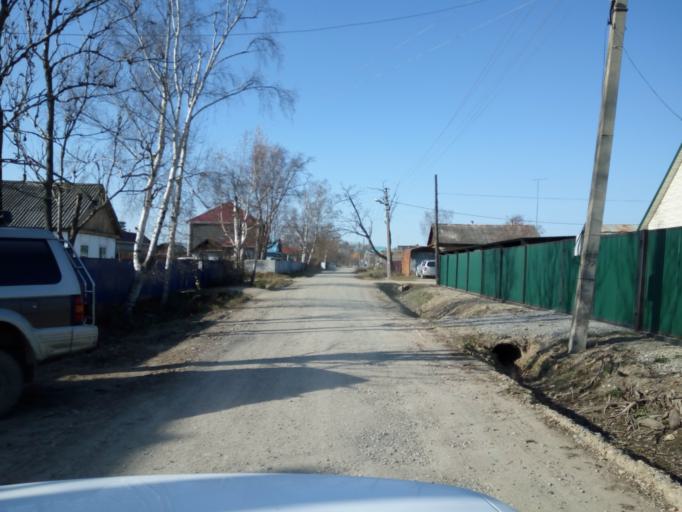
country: RU
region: Primorskiy
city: Dal'nerechensk
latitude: 45.9237
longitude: 133.7330
